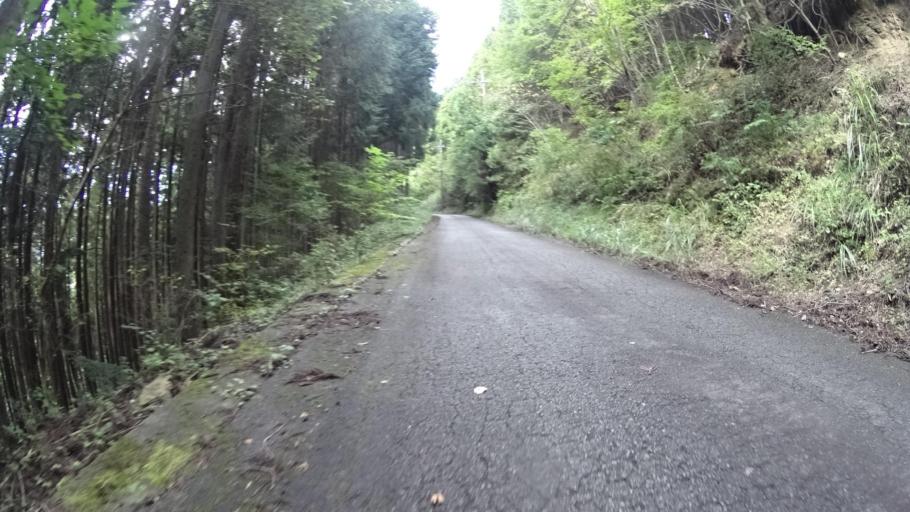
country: JP
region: Yamanashi
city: Uenohara
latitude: 35.7471
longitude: 139.0559
